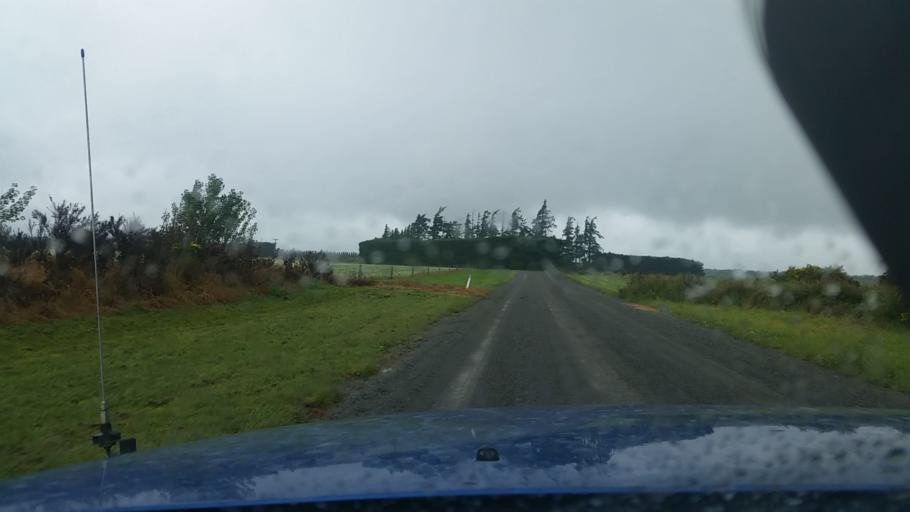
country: NZ
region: Canterbury
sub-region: Ashburton District
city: Methven
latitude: -43.6598
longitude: 171.8066
